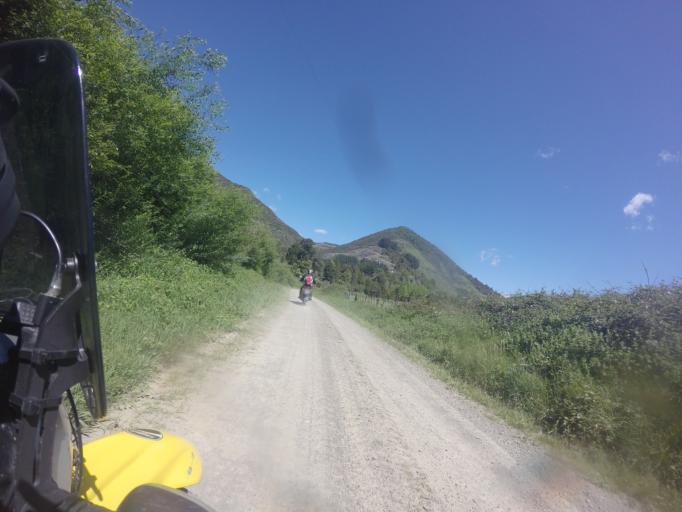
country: NZ
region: Bay of Plenty
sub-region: Opotiki District
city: Opotiki
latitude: -38.2995
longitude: 177.3335
